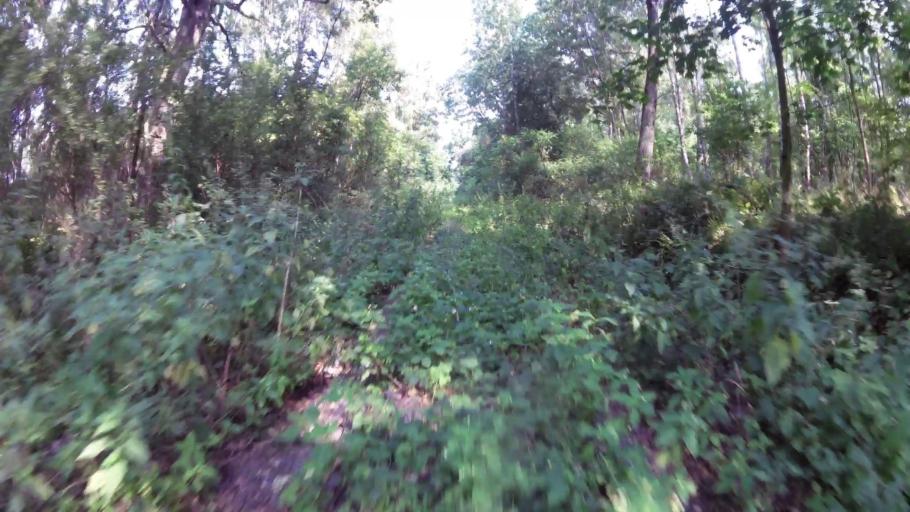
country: PL
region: West Pomeranian Voivodeship
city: Trzcinsko Zdroj
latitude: 52.9109
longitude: 14.5476
